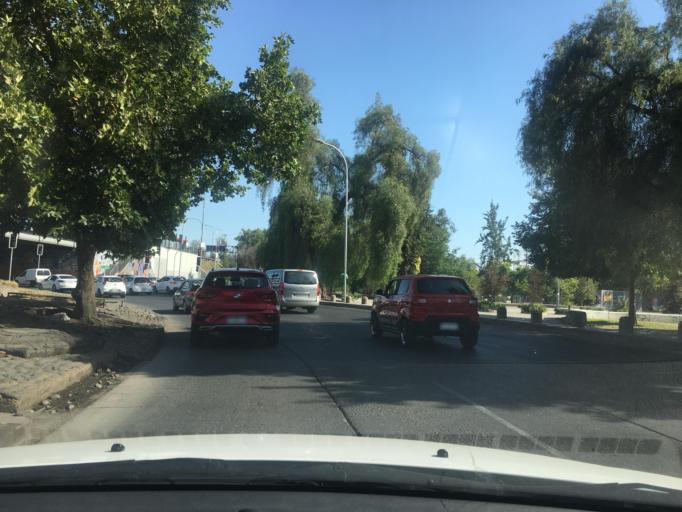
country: CL
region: Santiago Metropolitan
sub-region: Provincia de Santiago
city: Santiago
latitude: -33.4601
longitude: -70.6577
